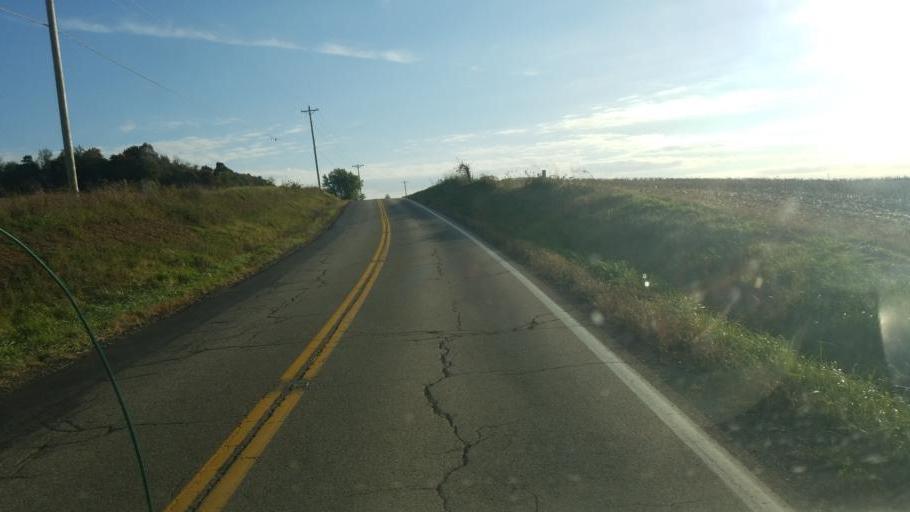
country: US
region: Ohio
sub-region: Wayne County
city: Shreve
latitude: 40.6082
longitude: -82.1034
